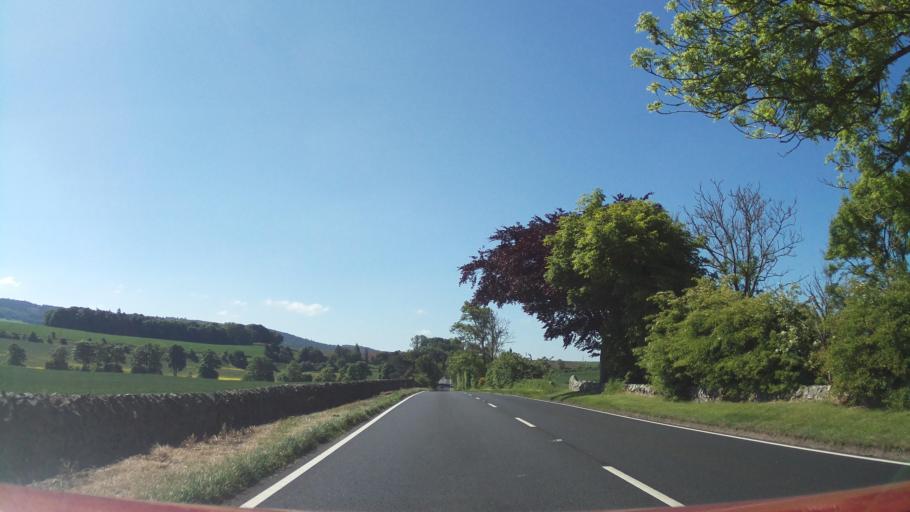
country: GB
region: Scotland
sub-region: Fife
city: Balmullo
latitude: 56.3537
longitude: -2.9414
